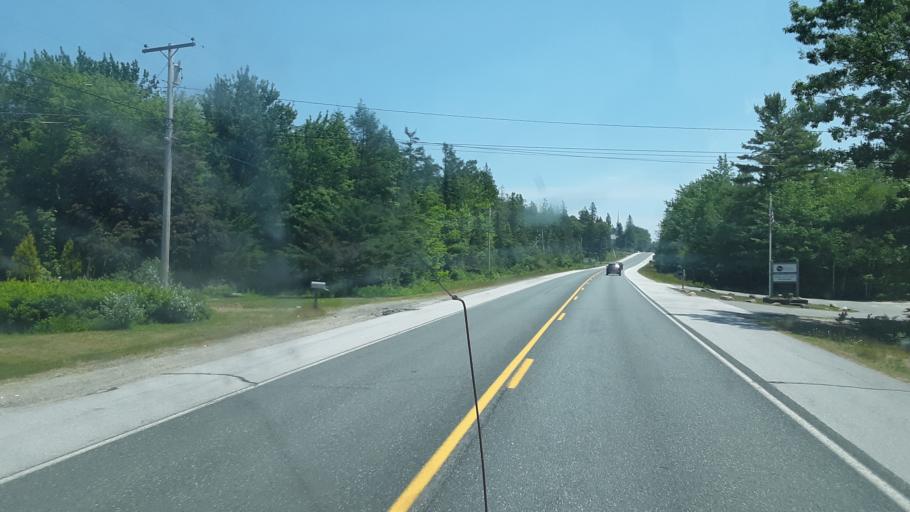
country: US
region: Maine
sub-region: Hancock County
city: Hancock
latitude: 44.5327
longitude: -68.2659
